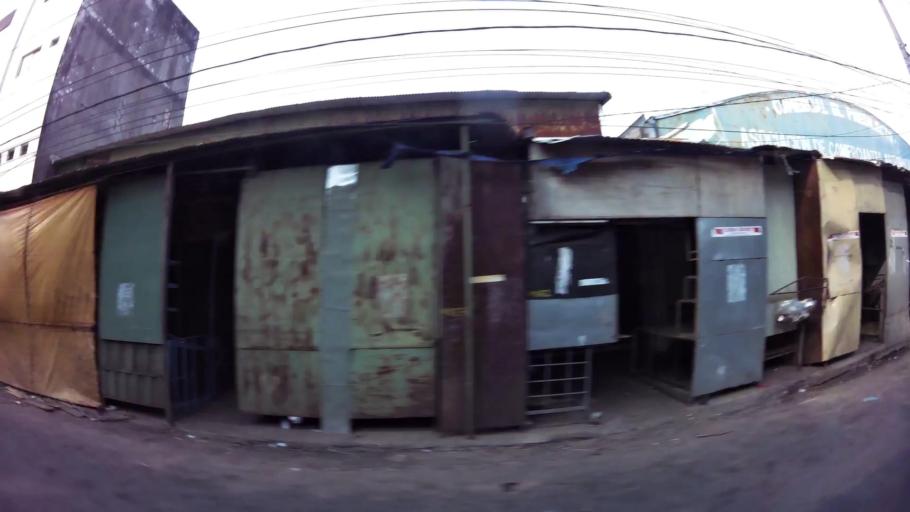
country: PY
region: Asuncion
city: Asuncion
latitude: -25.3013
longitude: -57.6238
